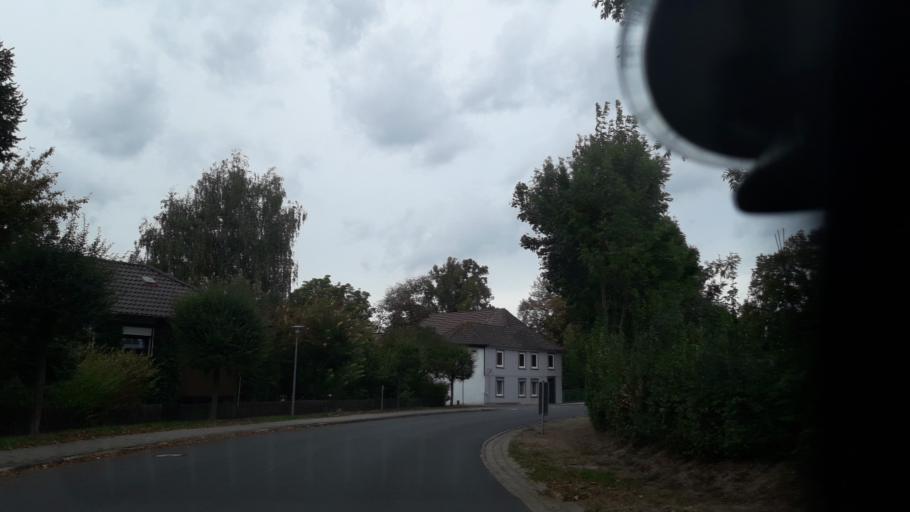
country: DE
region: Lower Saxony
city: Werlaburgdorf
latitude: 52.0479
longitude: 10.5395
